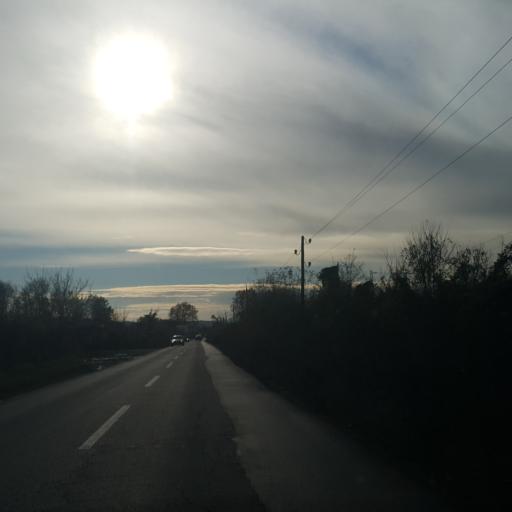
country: RS
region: Central Serbia
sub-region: Belgrade
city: Lazarevac
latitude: 44.4140
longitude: 20.2724
